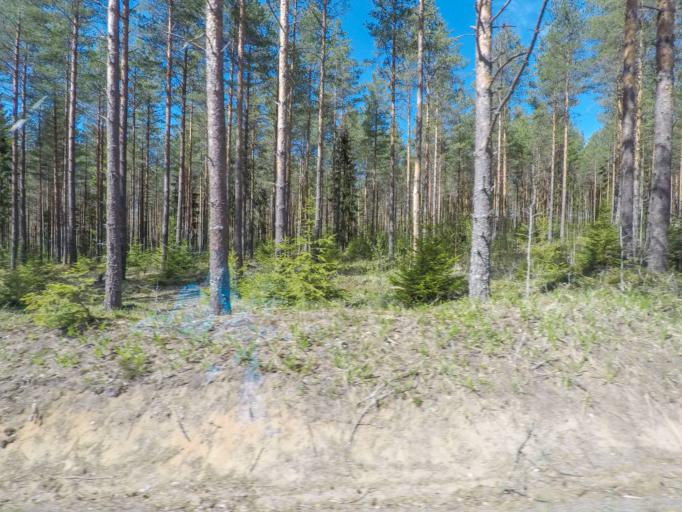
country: FI
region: Uusimaa
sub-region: Helsinki
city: Kaerkoelae
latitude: 60.4880
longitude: 23.8592
